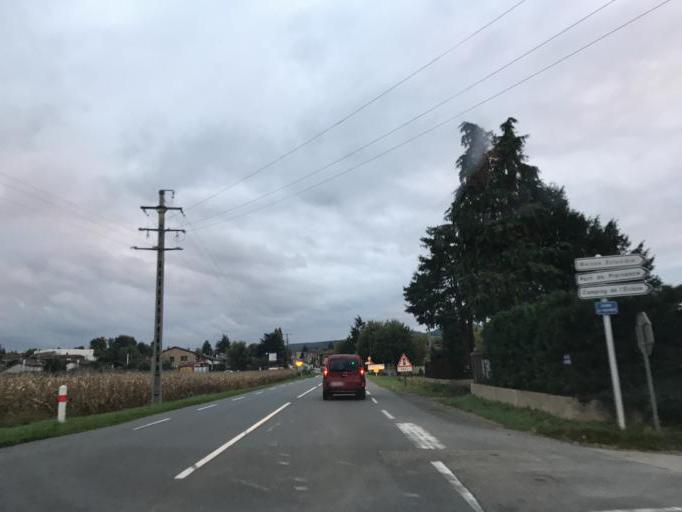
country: FR
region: Rhone-Alpes
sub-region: Departement de l'Ain
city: Massieux
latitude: 45.9106
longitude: 4.8160
